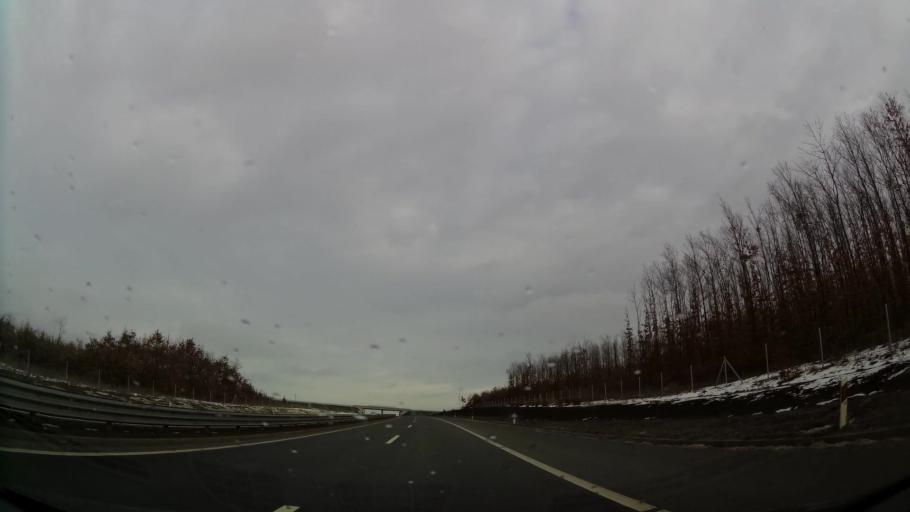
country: XK
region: Ferizaj
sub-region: Komuna e Ferizajt
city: Ferizaj
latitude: 42.3468
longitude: 21.2057
